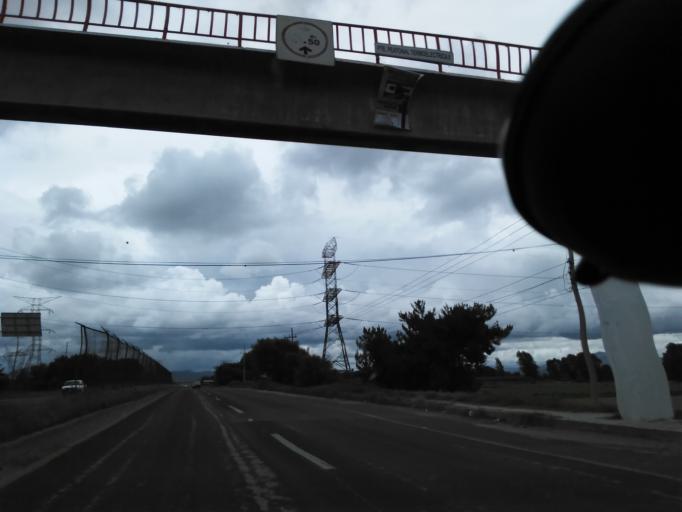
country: MX
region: Hidalgo
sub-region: Tula de Allende
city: Residencial Arboledas
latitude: 20.0619
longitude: -99.2778
